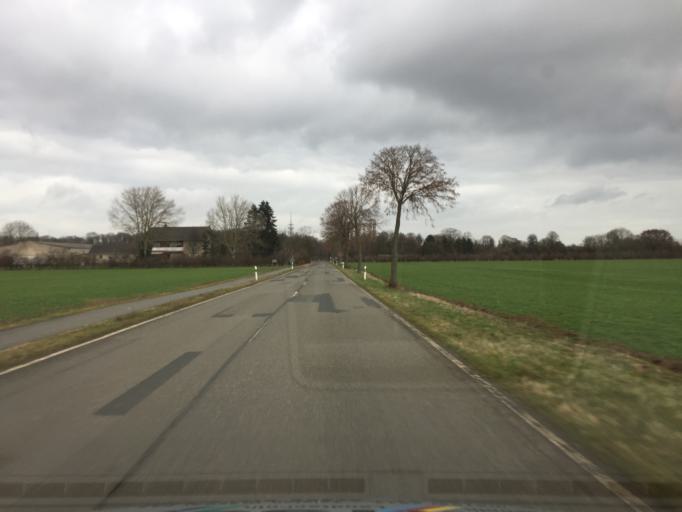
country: DE
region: Lower Saxony
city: Stolzenau
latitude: 52.5030
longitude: 9.0719
